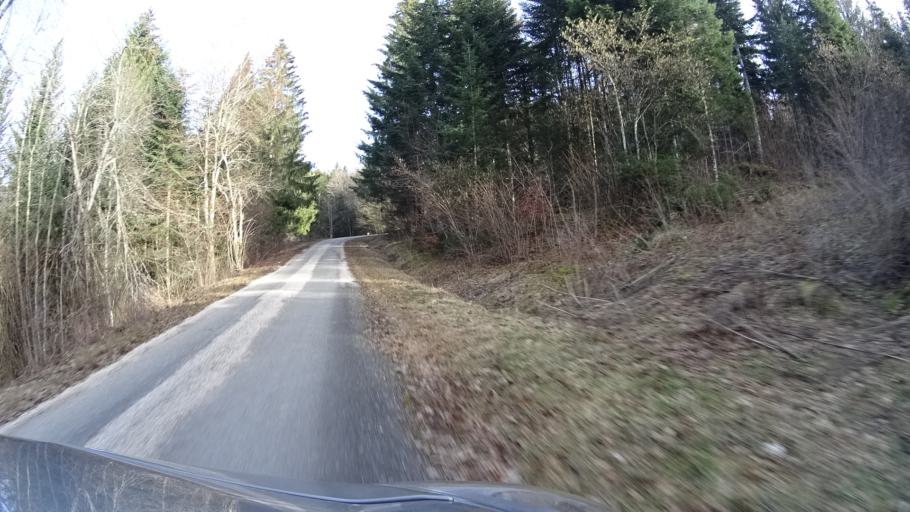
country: FR
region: Franche-Comte
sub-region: Departement du Doubs
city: Pontarlier
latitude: 46.8704
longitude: 6.2683
